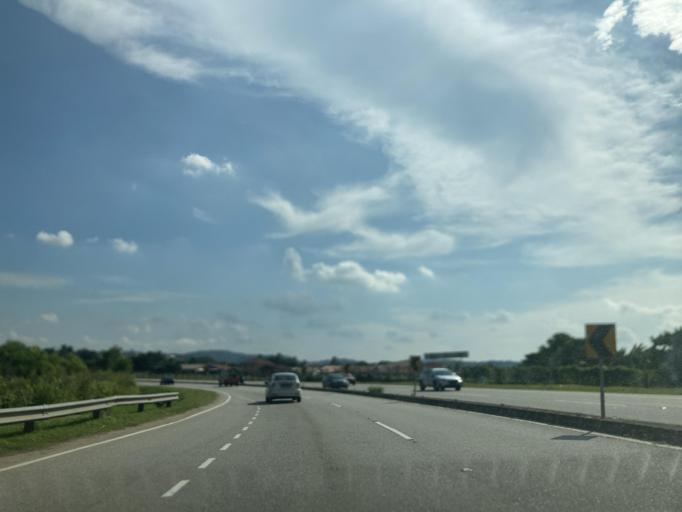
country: MY
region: Selangor
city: Kampung Baru Subang
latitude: 3.1494
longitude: 101.5399
